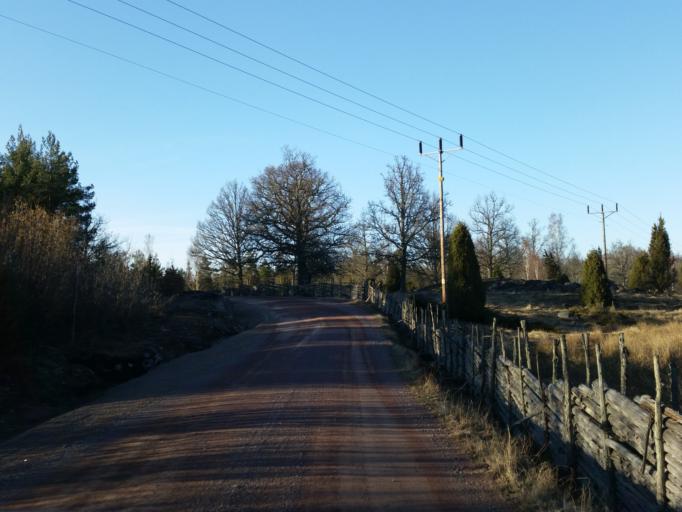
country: SE
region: Kalmar
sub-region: Oskarshamns Kommun
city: Oskarshamn
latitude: 57.3360
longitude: 16.4740
